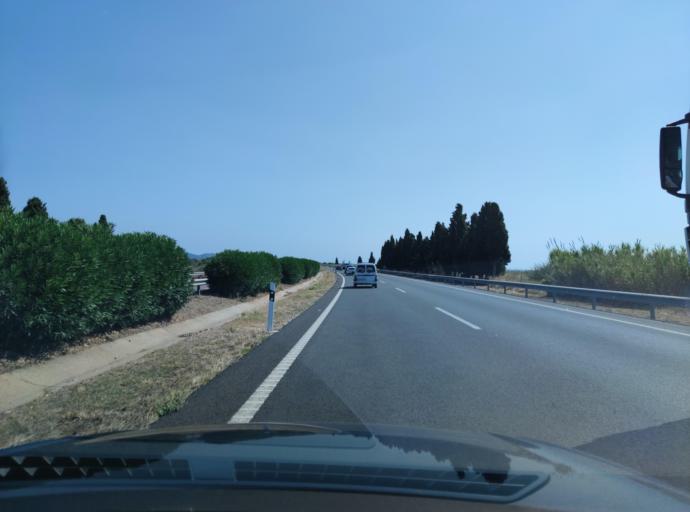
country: ES
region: Valencia
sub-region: Provincia de Valencia
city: Faura
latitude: 39.7060
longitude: -0.2452
